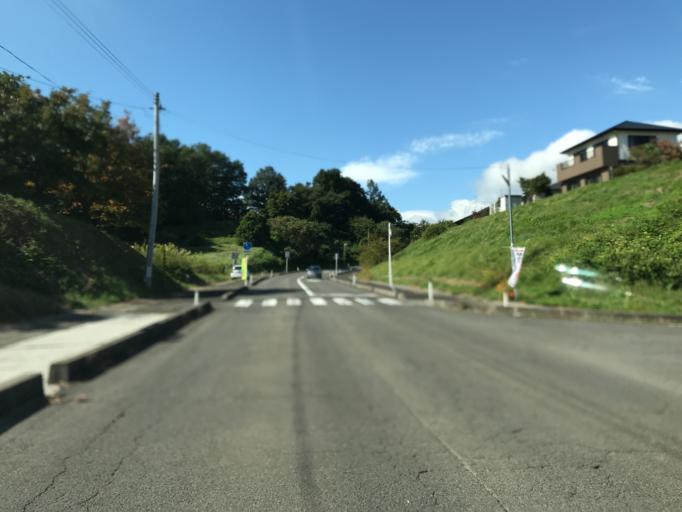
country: JP
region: Fukushima
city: Fukushima-shi
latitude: 37.6555
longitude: 140.5296
